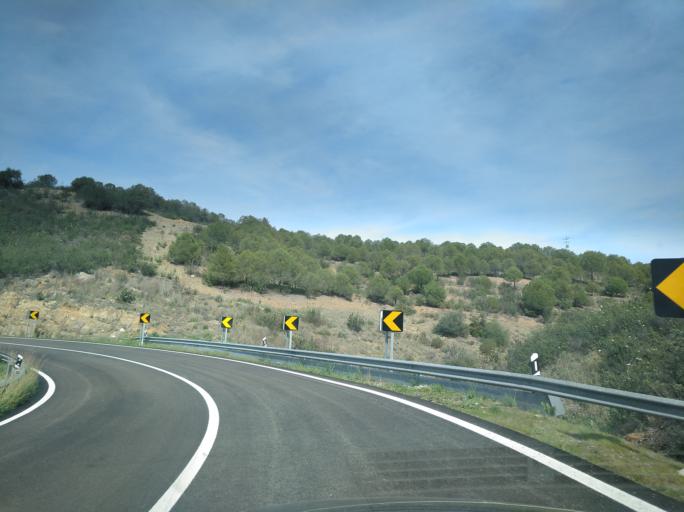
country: PT
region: Faro
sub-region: Alcoutim
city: Alcoutim
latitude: 37.5102
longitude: -7.5825
